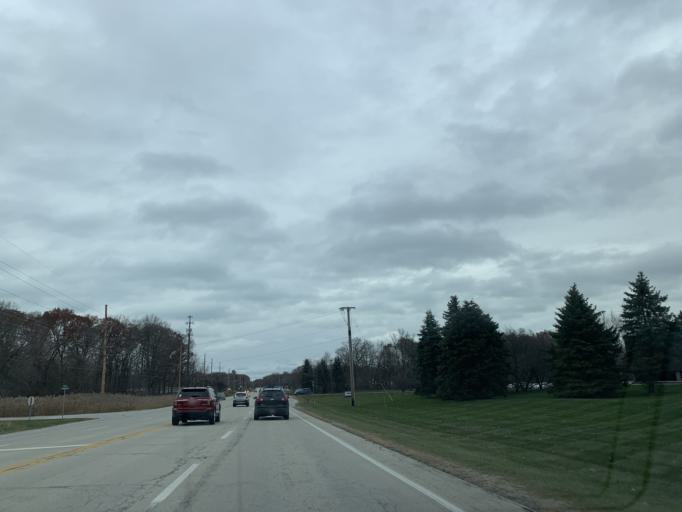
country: US
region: Indiana
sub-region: LaPorte County
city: Long Beach
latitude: 41.7321
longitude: -86.8261
